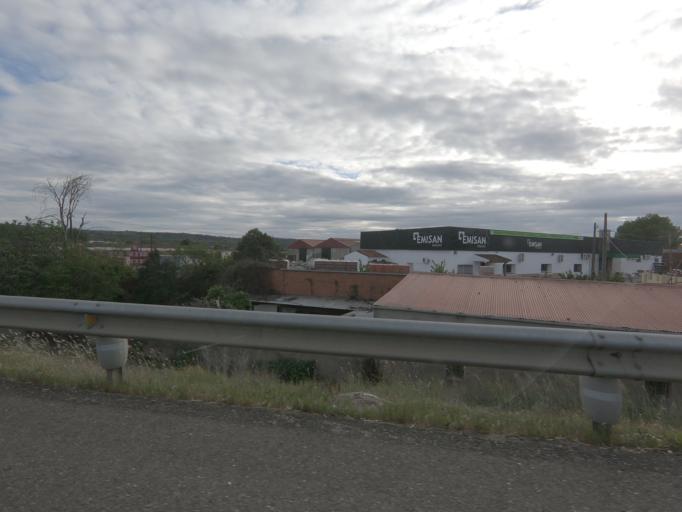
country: ES
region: Extremadura
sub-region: Provincia de Caceres
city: Coria
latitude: 39.9751
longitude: -6.5260
